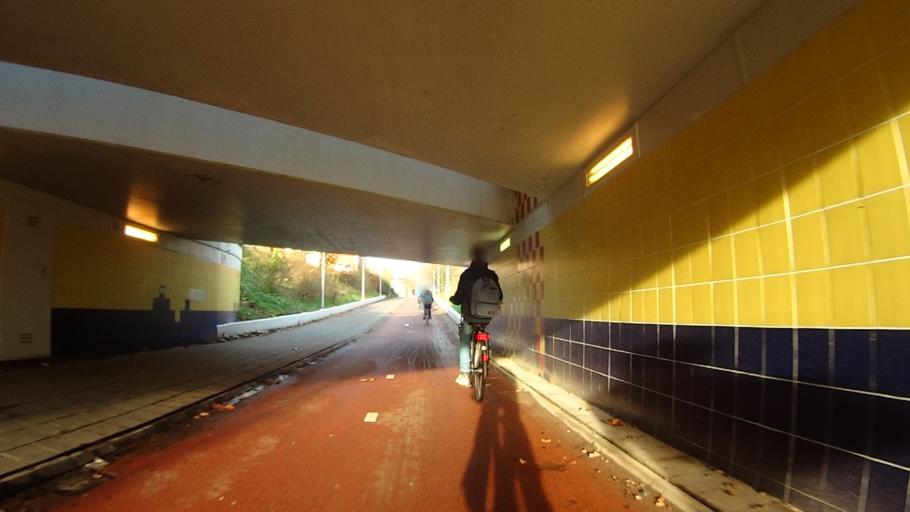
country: NL
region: Utrecht
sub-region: Gemeente Amersfoort
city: Randenbroek
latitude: 52.1721
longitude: 5.4042
